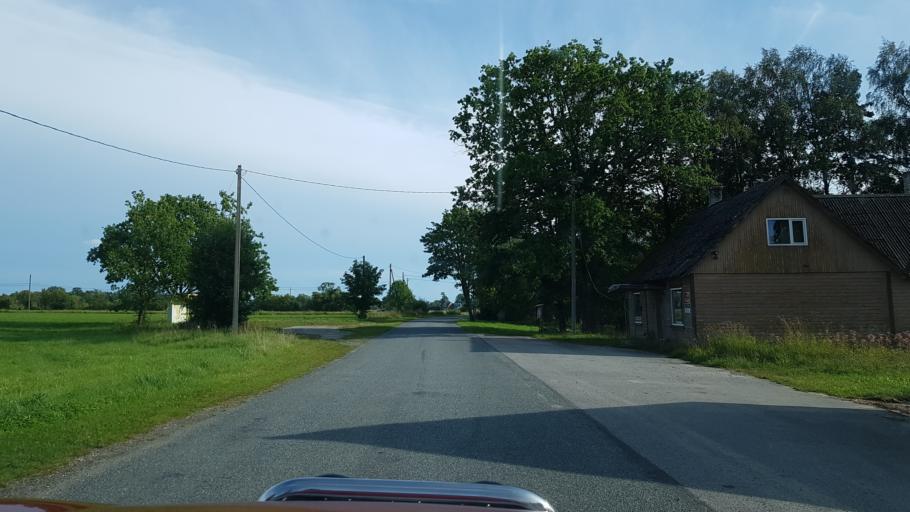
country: EE
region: Laeaene
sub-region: Lihula vald
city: Lihula
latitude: 58.4344
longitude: 24.0063
